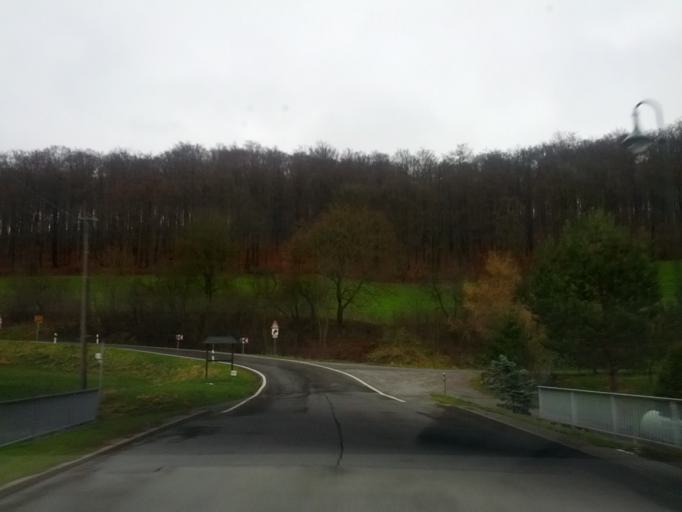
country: DE
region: Thuringia
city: Hallungen
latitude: 51.1381
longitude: 10.3294
